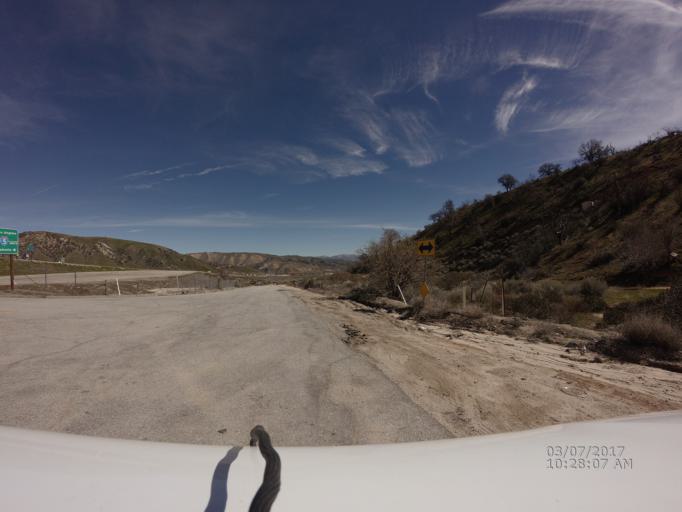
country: US
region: California
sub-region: Kern County
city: Lebec
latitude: 34.8170
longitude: -118.8814
